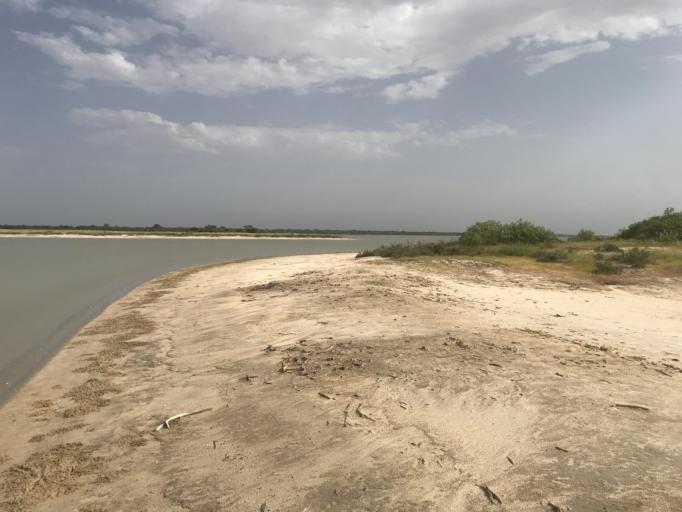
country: SN
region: Saint-Louis
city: Saint-Louis
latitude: 15.9280
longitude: -16.4637
